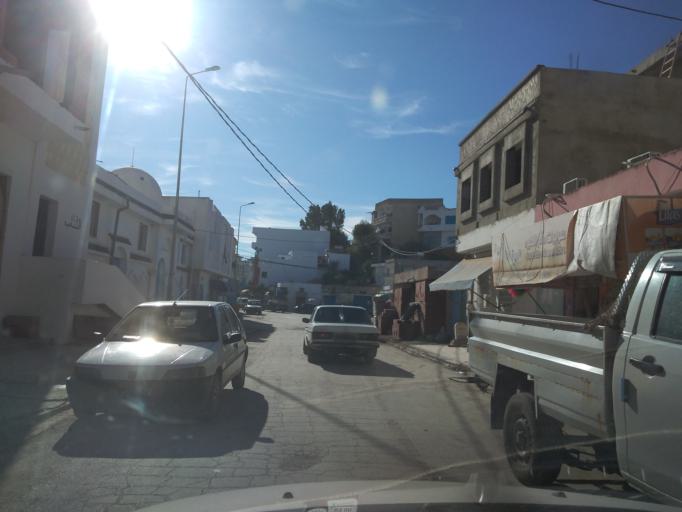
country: TN
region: Ariana
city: Qal'at al Andalus
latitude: 37.0634
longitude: 10.1188
